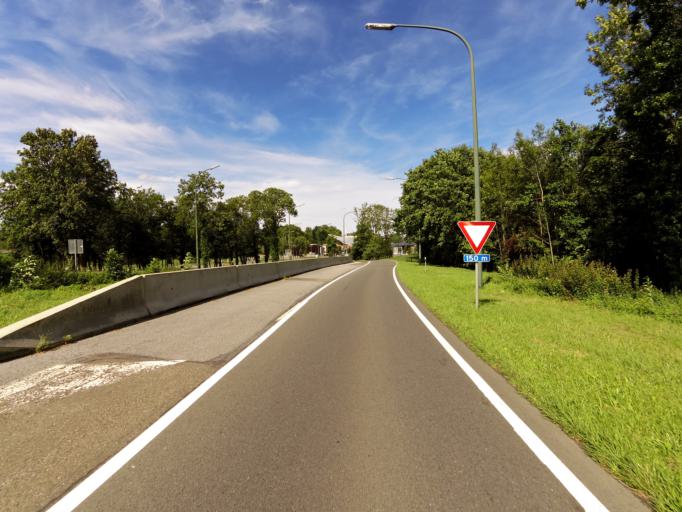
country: BE
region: Wallonia
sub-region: Province du Luxembourg
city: Marche-en-Famenne
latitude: 50.2242
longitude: 5.3392
